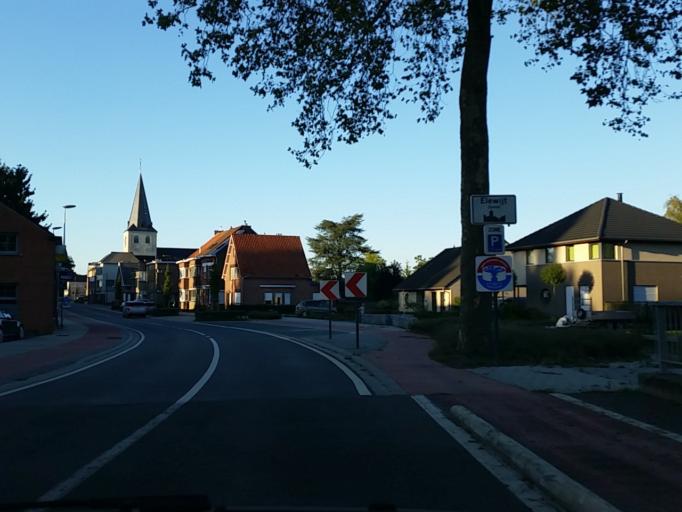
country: BE
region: Flanders
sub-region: Provincie Vlaams-Brabant
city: Steenokkerzeel
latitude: 50.9580
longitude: 4.4978
